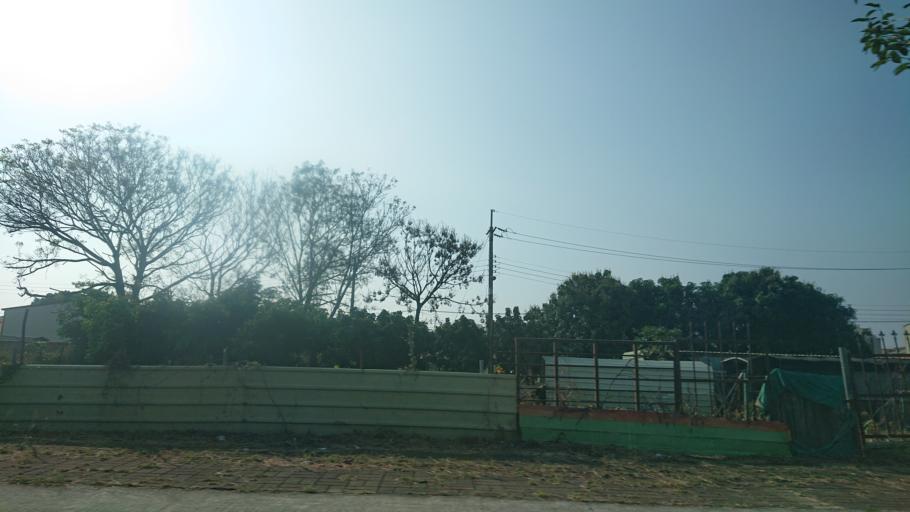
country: TW
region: Taiwan
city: Xinying
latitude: 23.3368
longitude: 120.2504
